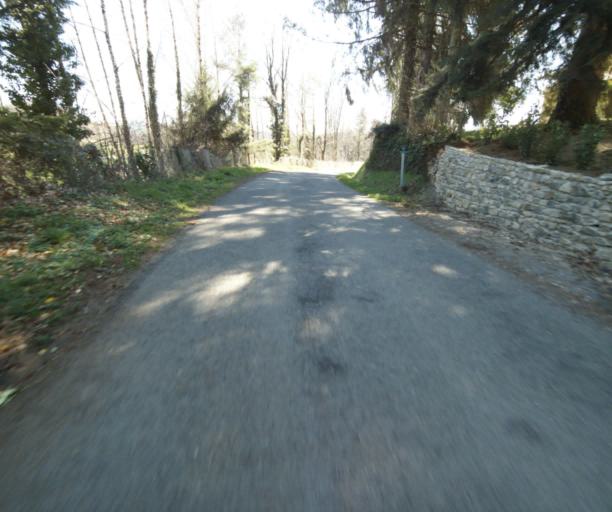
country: FR
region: Limousin
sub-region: Departement de la Correze
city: Saint-Clement
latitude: 45.3008
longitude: 1.7019
